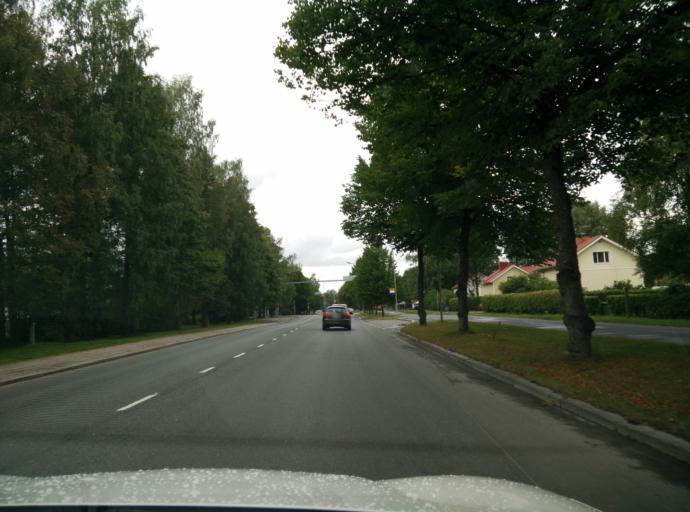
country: FI
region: Haeme
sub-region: Haemeenlinna
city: Haemeenlinna
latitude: 60.9997
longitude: 24.4313
